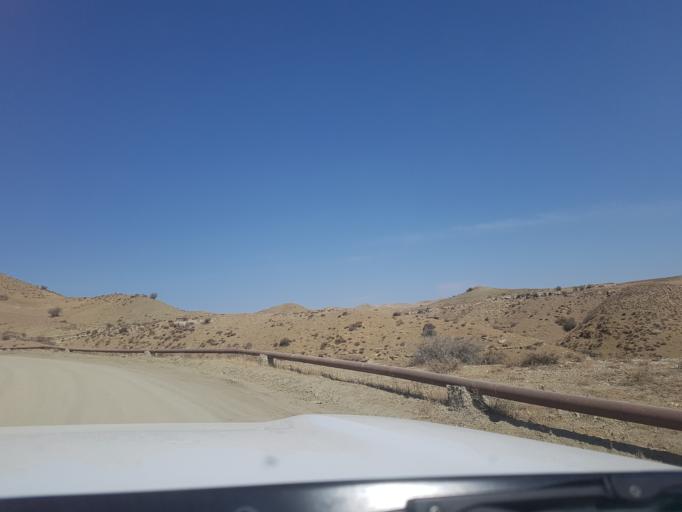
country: TM
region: Ahal
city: Baharly
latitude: 38.2413
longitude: 56.8903
